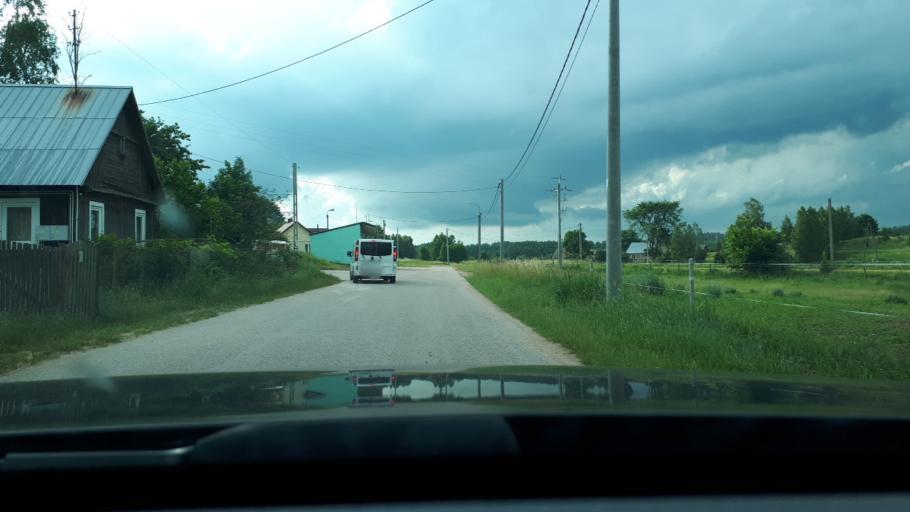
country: PL
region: Podlasie
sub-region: Powiat bialostocki
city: Dobrzyniewo Duze
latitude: 53.2740
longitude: 22.9881
